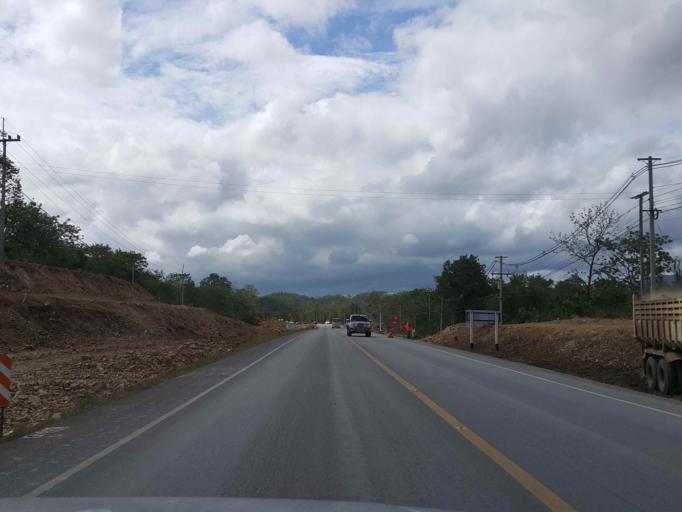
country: TH
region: Tak
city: Tak
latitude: 16.7940
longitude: 99.0116
